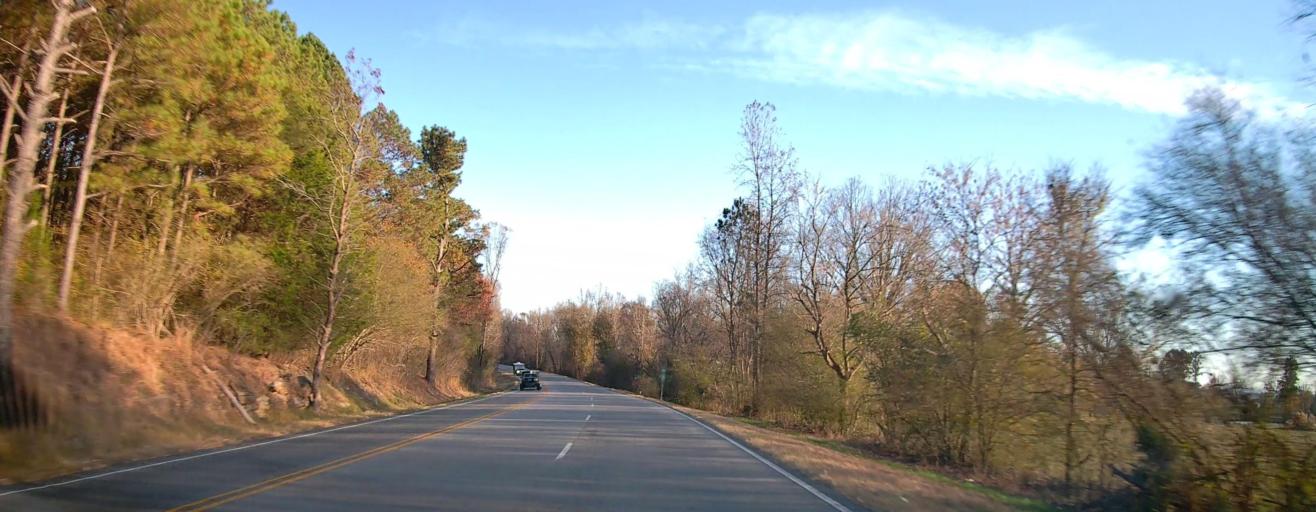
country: US
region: Alabama
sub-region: Blount County
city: Blountsville
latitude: 34.1445
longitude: -86.4495
